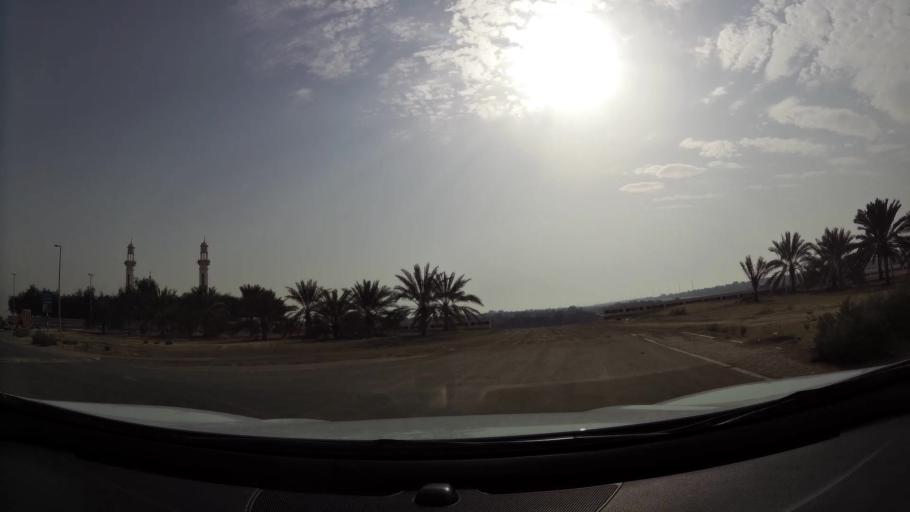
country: AE
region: Abu Dhabi
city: Abu Dhabi
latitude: 24.2369
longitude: 54.7251
